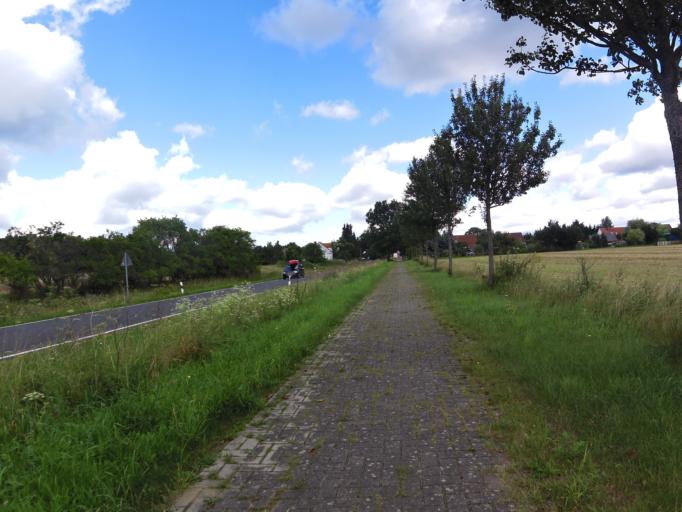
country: DE
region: Brandenburg
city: Lychen
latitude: 53.2650
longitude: 13.3477
